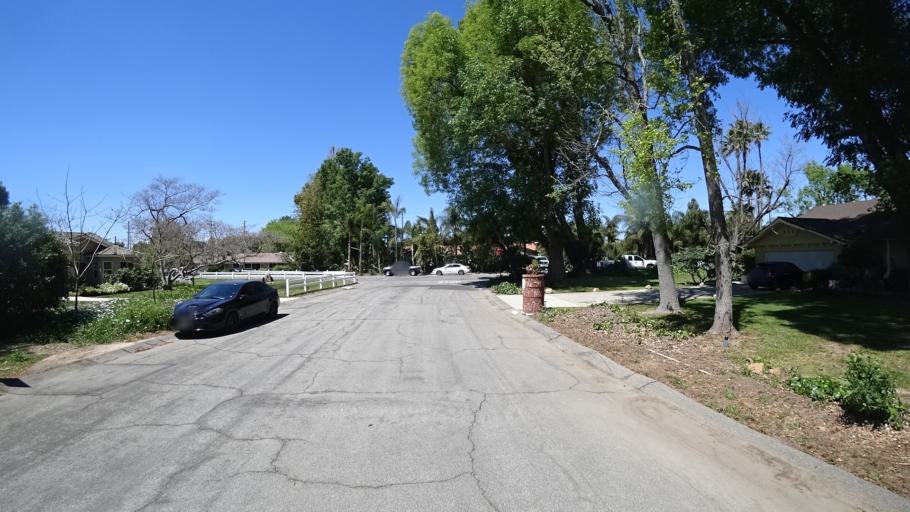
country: US
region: California
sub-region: Ventura County
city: Thousand Oaks
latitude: 34.1972
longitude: -118.8520
